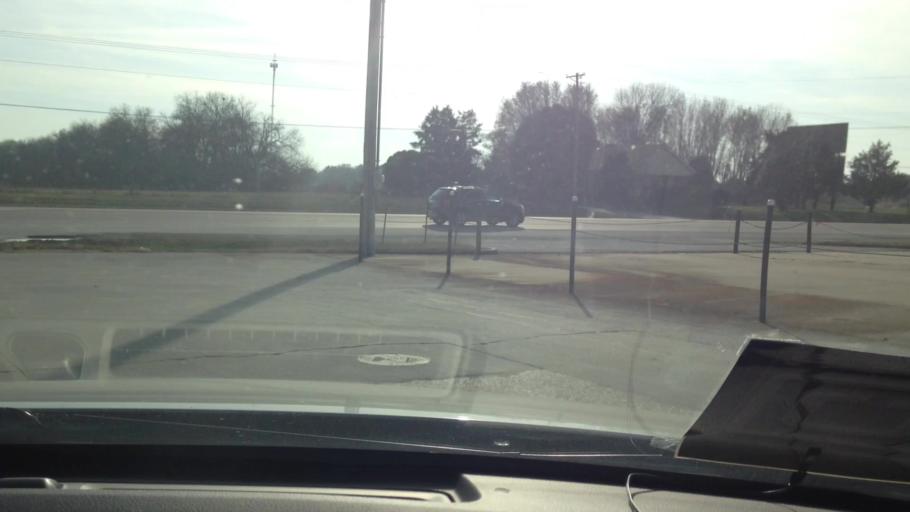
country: US
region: Missouri
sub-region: Henry County
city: Clinton
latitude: 38.3896
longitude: -93.7967
